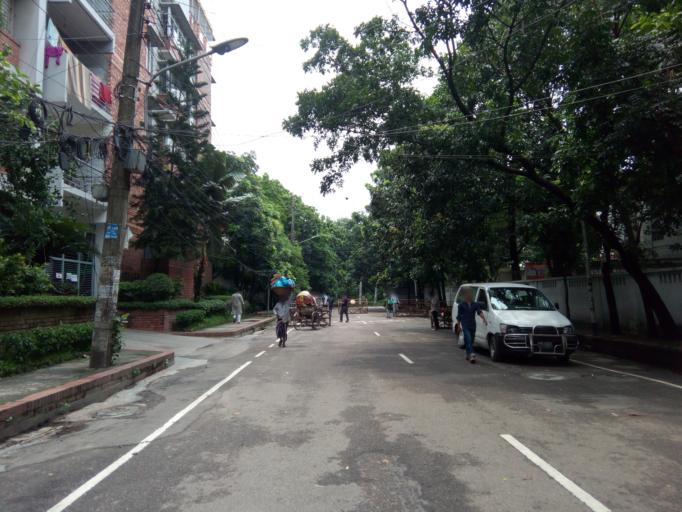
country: BD
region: Dhaka
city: Azimpur
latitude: 23.7421
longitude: 90.3777
